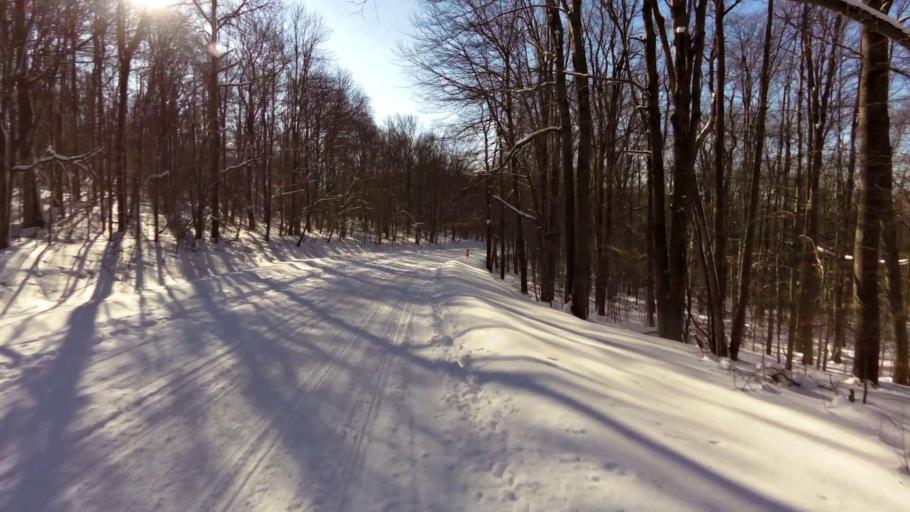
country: US
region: New York
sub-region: Cattaraugus County
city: Salamanca
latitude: 42.0418
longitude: -78.7811
